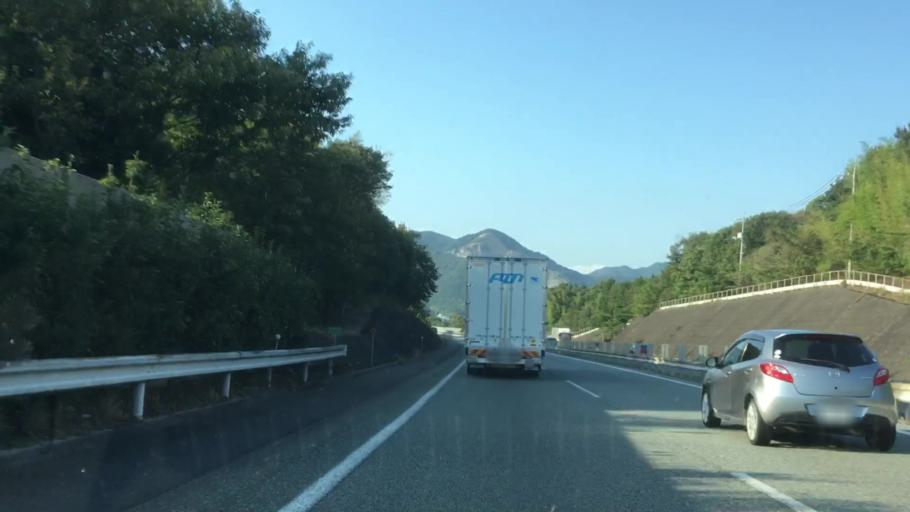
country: JP
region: Yamaguchi
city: Hofu
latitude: 34.0636
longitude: 131.5017
